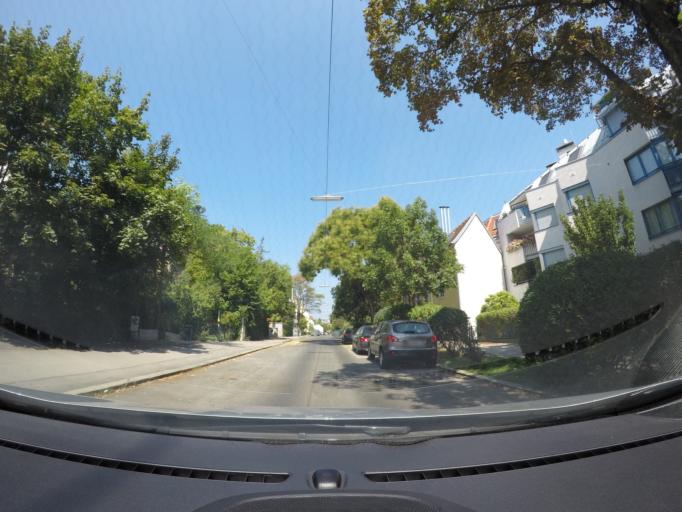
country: AT
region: Lower Austria
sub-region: Politischer Bezirk Modling
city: Perchtoldsdorf
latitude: 48.1888
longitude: 16.2722
